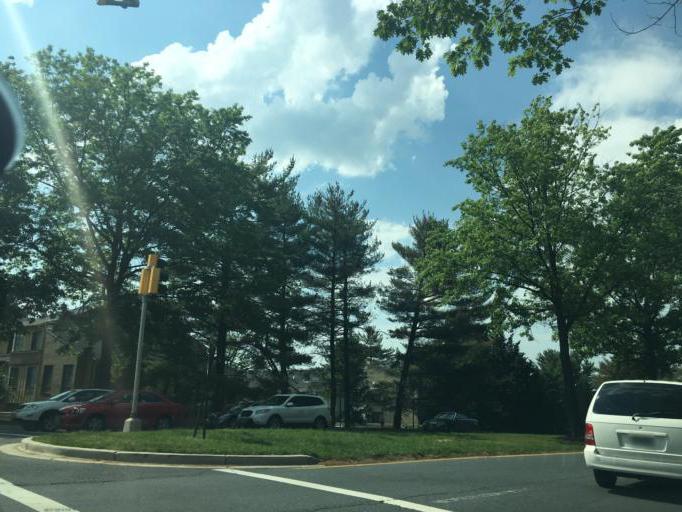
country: US
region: Maryland
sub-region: Montgomery County
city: Montgomery Village
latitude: 39.1746
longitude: -77.2033
